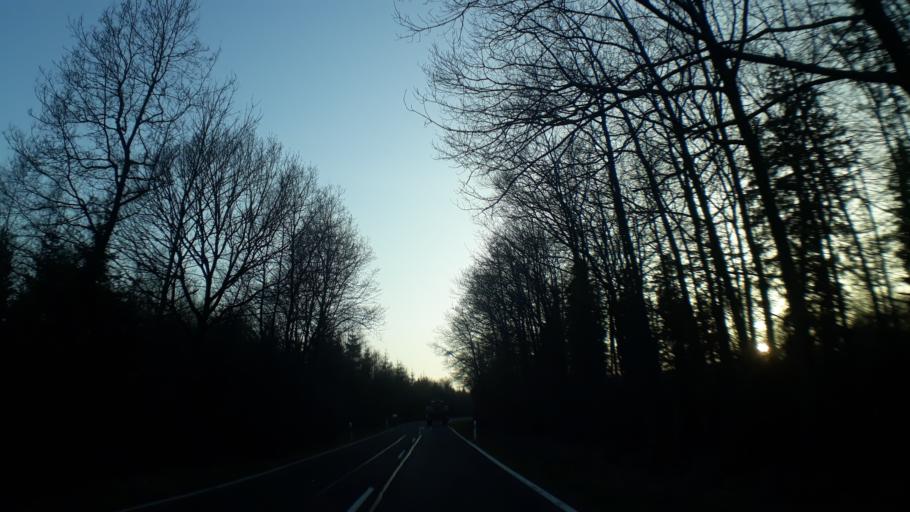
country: DE
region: Rheinland-Pfalz
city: Ohlenhard
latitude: 50.4738
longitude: 6.7432
